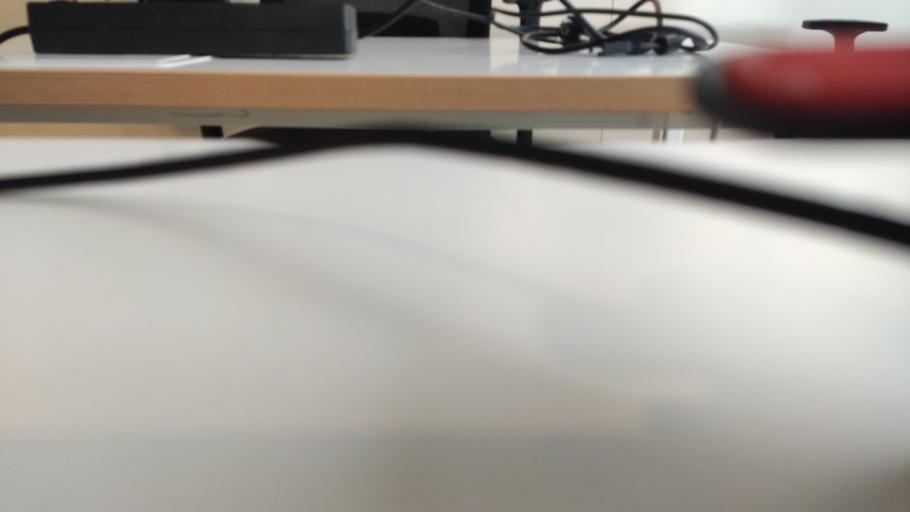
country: RU
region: Moskovskaya
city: Rogachevo
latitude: 56.4106
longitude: 37.0591
